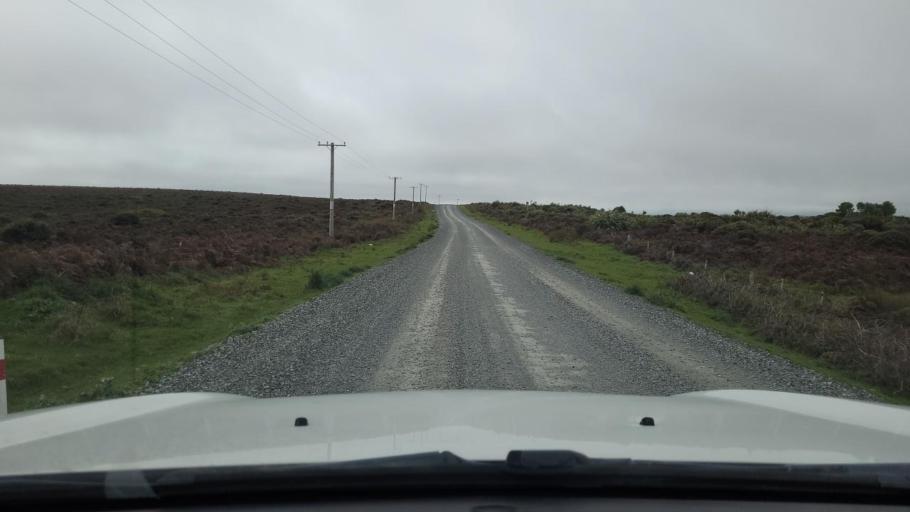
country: NZ
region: Chatham Islands
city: Waitangi
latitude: -43.8273
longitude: -176.4982
